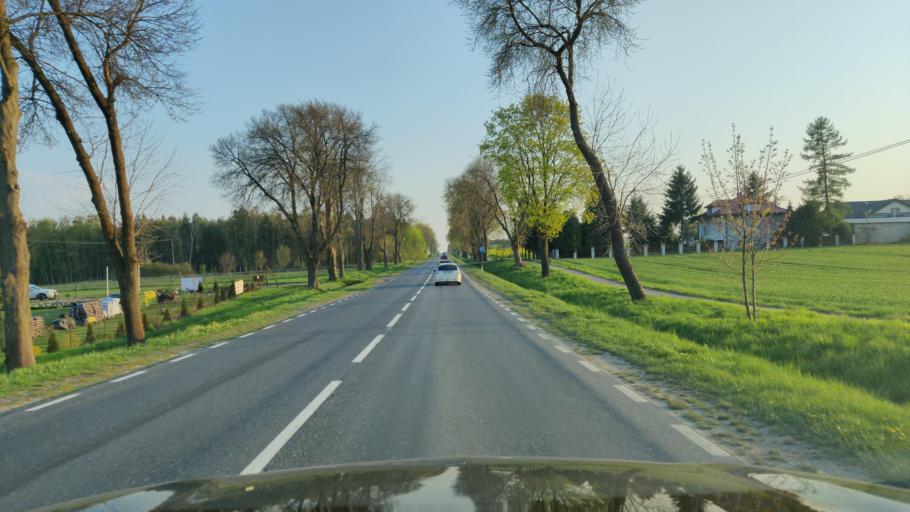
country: PL
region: Masovian Voivodeship
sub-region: Powiat legionowski
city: Serock
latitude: 52.5805
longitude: 21.0970
